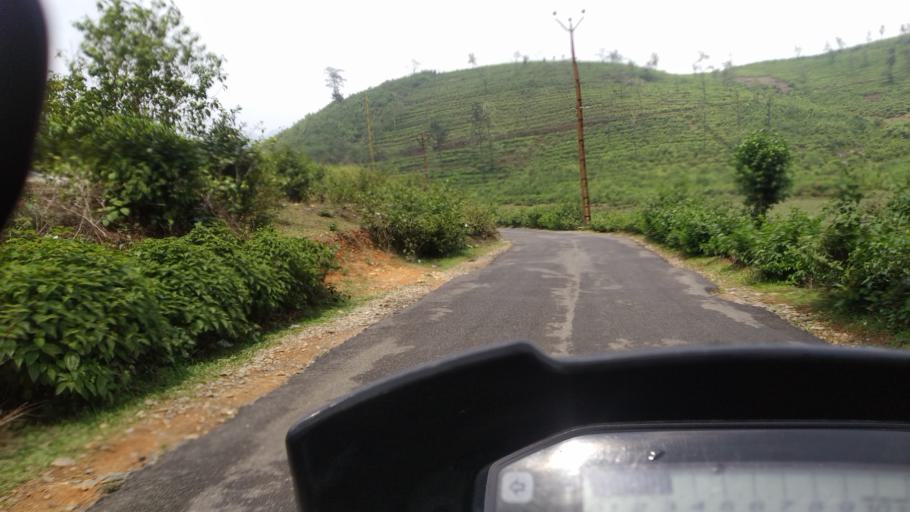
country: IN
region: Kerala
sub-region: Kottayam
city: Erattupetta
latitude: 9.6351
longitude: 76.9511
